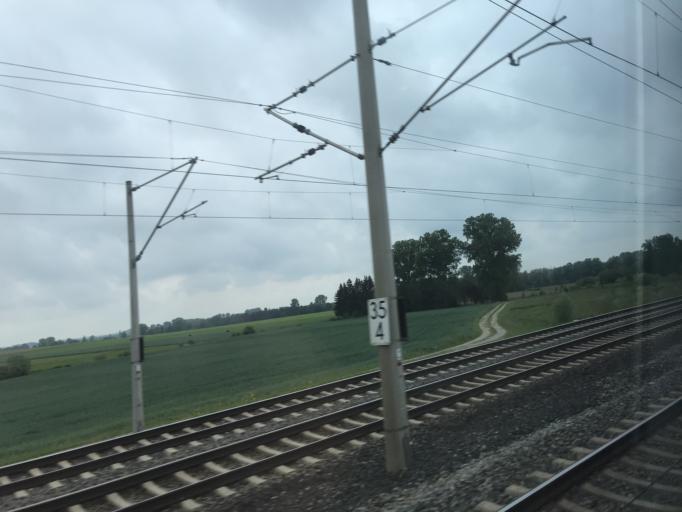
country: DE
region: Bavaria
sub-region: Upper Bavaria
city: Hattenhofen
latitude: 48.2189
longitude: 11.1152
